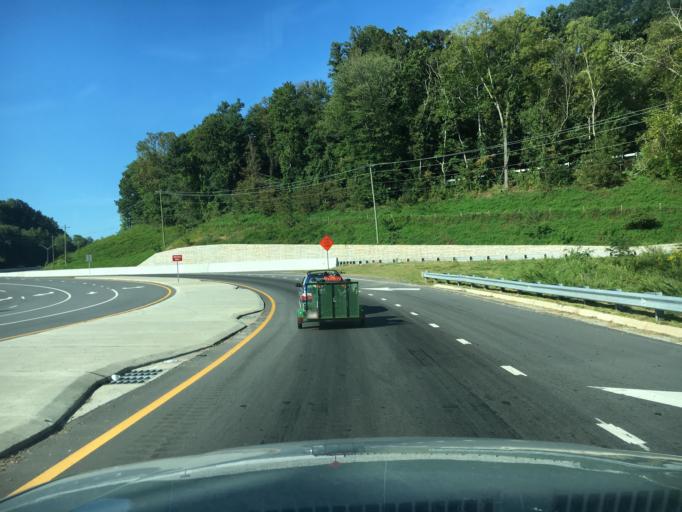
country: US
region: North Carolina
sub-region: Haywood County
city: Lake Junaluska
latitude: 35.5246
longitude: -82.9582
